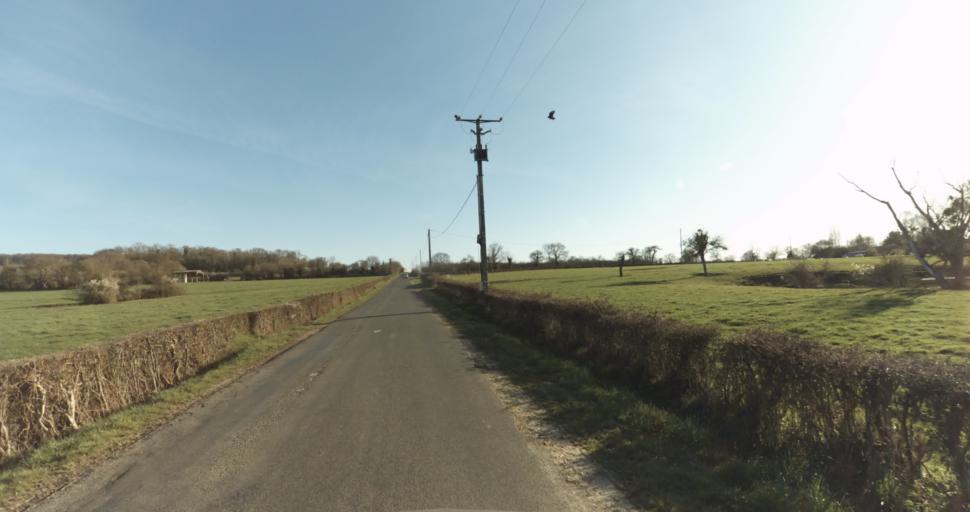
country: FR
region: Lower Normandy
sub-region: Departement du Calvados
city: Saint-Pierre-sur-Dives
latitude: 48.9564
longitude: 0.0497
